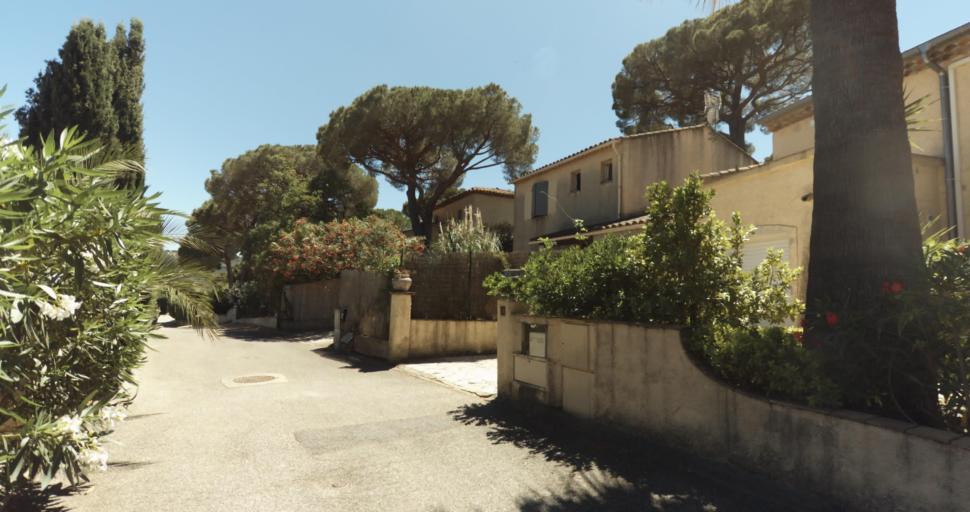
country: FR
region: Provence-Alpes-Cote d'Azur
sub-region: Departement du Var
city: Gassin
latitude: 43.2486
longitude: 6.5689
